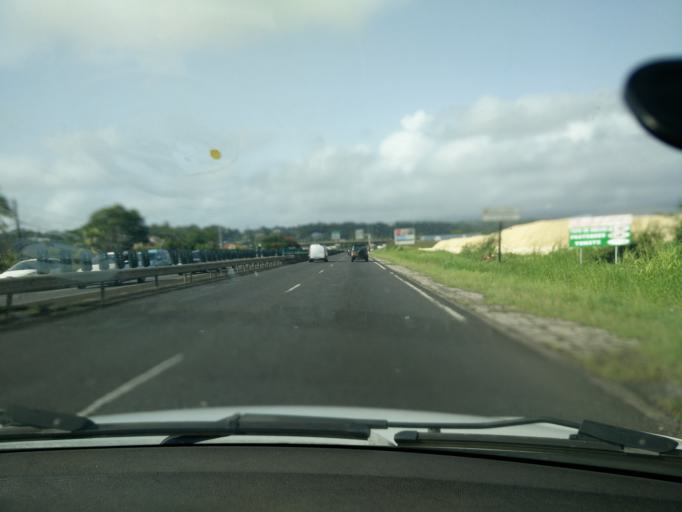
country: GP
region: Guadeloupe
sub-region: Guadeloupe
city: Petit-Bourg
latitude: 16.2053
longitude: -61.6046
